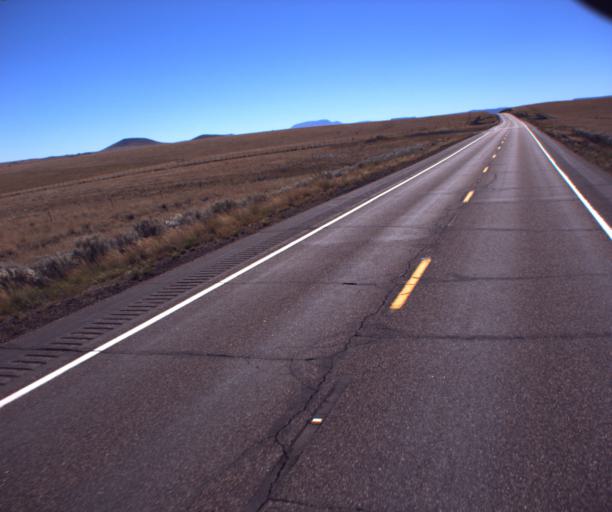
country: US
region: Arizona
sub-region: Apache County
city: Springerville
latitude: 34.3067
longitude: -109.3787
